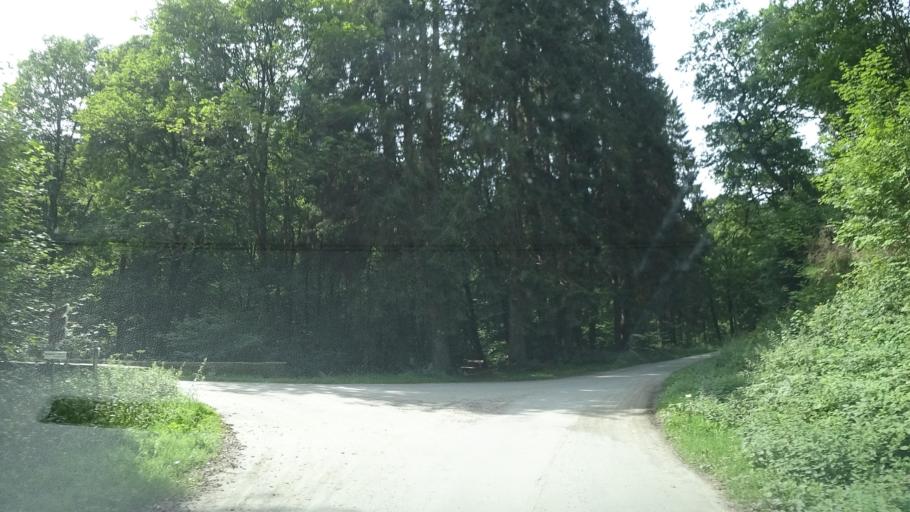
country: BE
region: Wallonia
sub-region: Province du Luxembourg
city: Herbeumont
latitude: 49.7721
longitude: 5.2552
